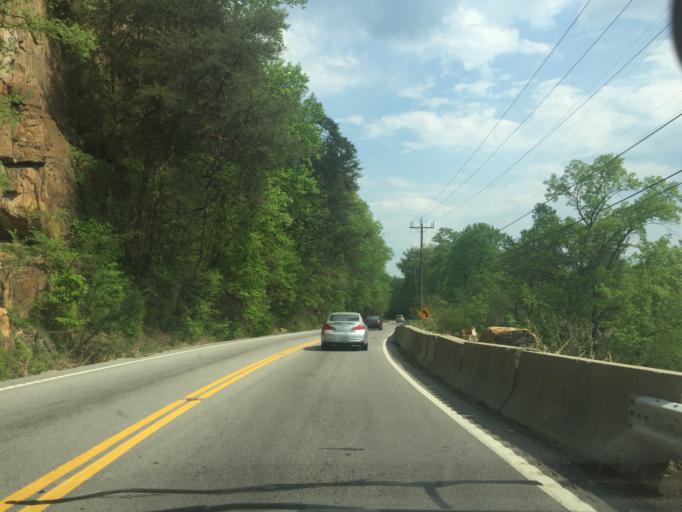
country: US
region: Tennessee
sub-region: Hamilton County
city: Signal Mountain
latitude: 35.1120
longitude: -85.3539
